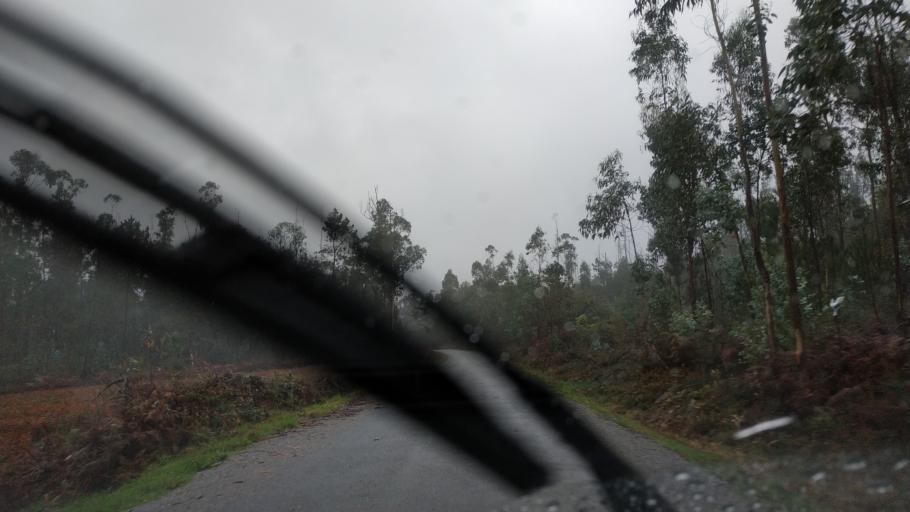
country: ES
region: Galicia
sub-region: Provincia da Coruna
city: Negreira
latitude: 42.9106
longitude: -8.7676
